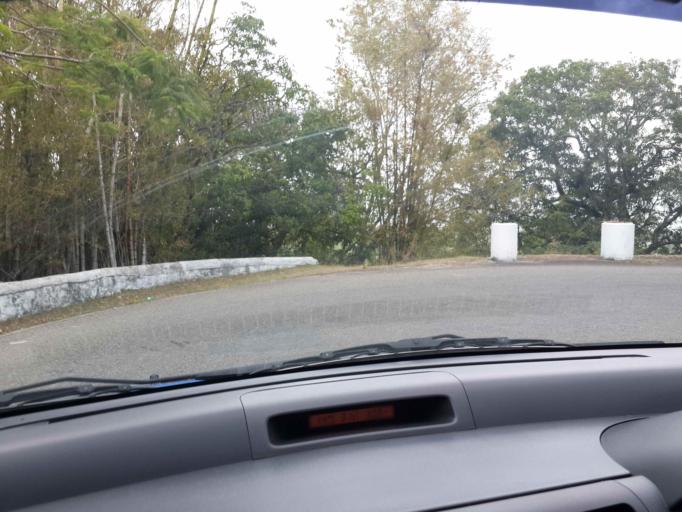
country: LC
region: Castries Quarter
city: Castries
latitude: 14.0064
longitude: -60.9982
